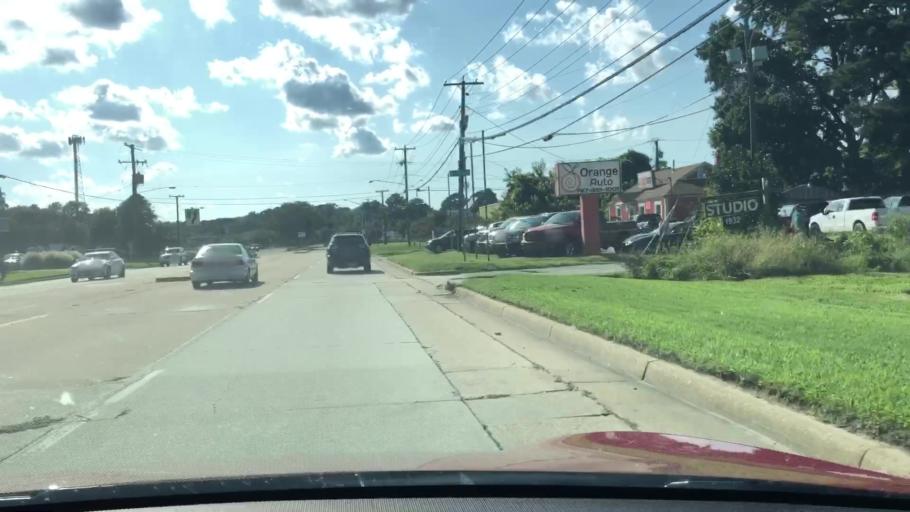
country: US
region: Virginia
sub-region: City of Virginia Beach
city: Virginia Beach
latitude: 36.8441
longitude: -76.0343
